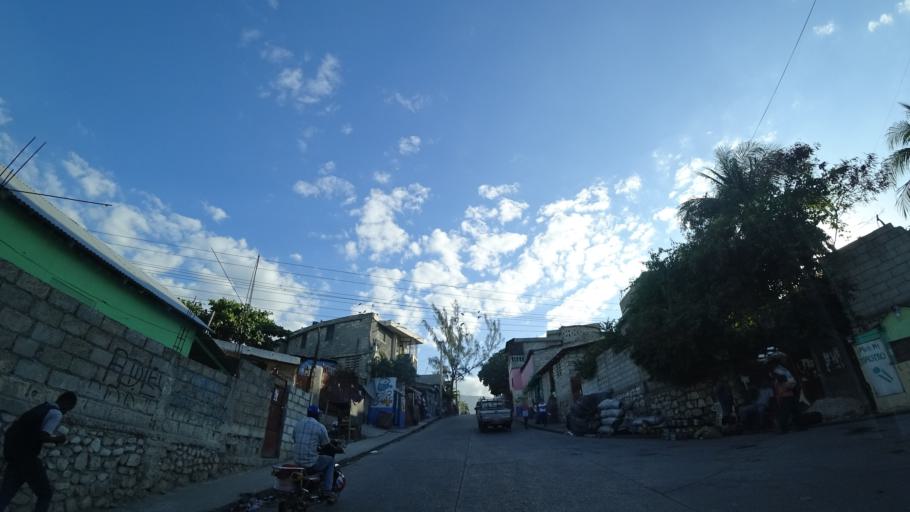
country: HT
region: Ouest
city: Delmas 73
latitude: 18.5480
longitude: -72.3149
